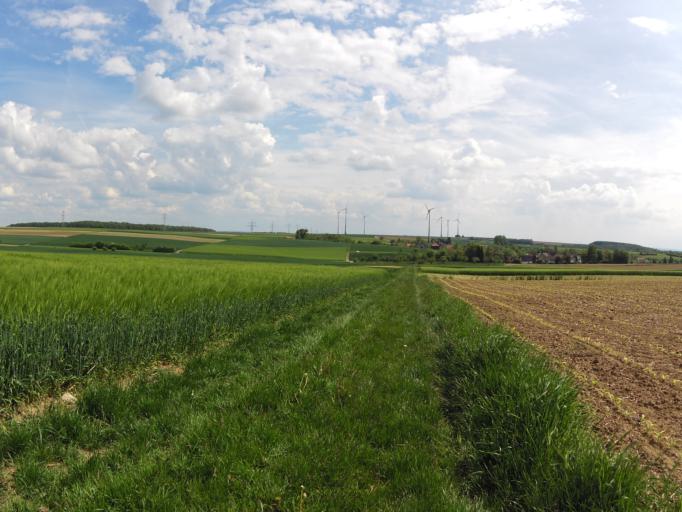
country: DE
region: Bavaria
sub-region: Regierungsbezirk Unterfranken
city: Theilheim
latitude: 49.7402
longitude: 10.0320
